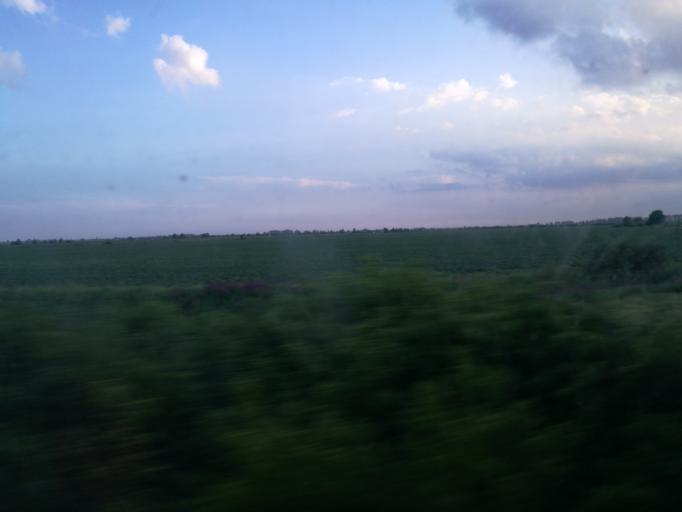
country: RO
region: Dambovita
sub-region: Comuna Contesti
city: Balteni
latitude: 44.6504
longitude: 25.6841
